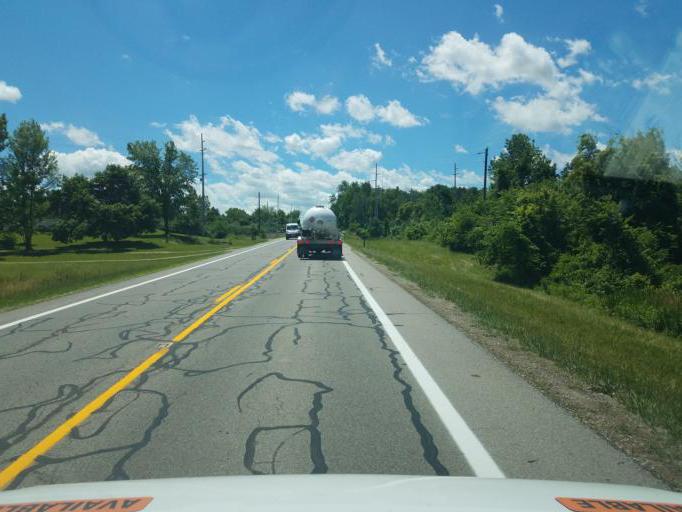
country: US
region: Ohio
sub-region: Crawford County
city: Galion
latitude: 40.6690
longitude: -82.8212
